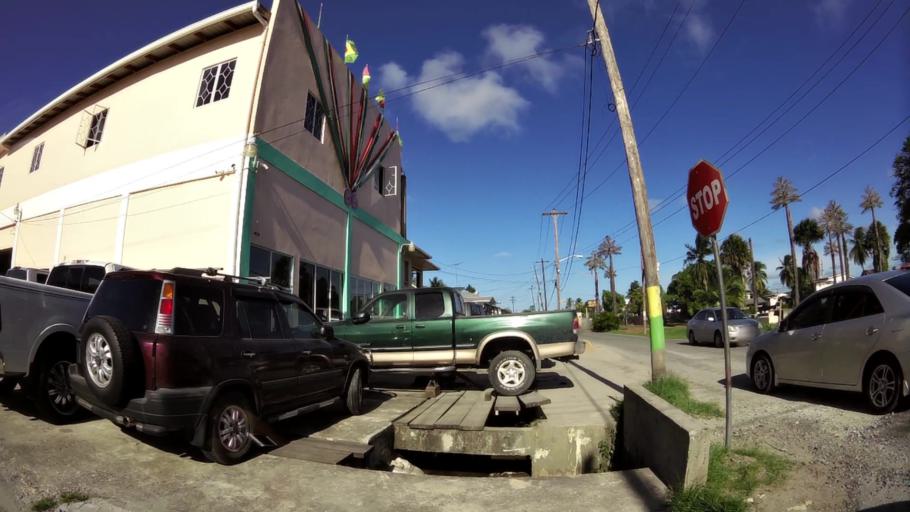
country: GY
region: Demerara-Mahaica
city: Georgetown
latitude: 6.8213
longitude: -58.1361
